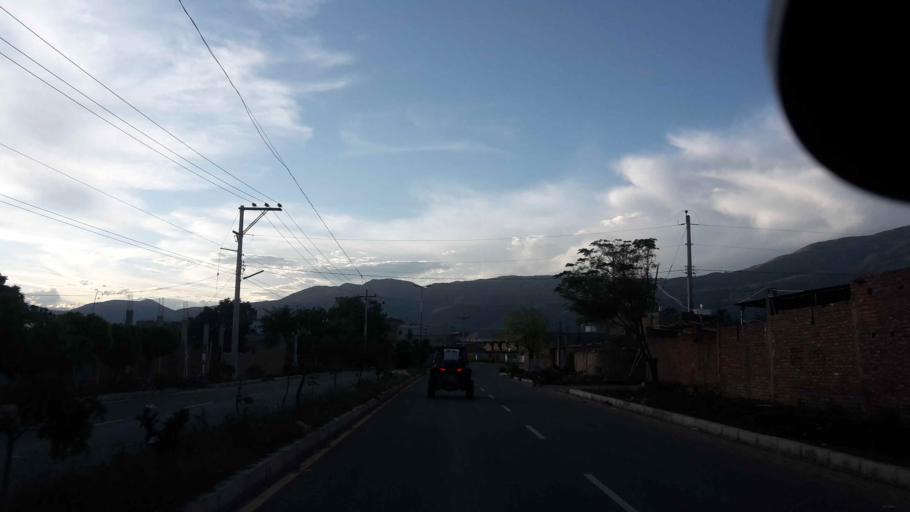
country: BO
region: Cochabamba
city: Punata
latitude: -17.5396
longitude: -65.8333
